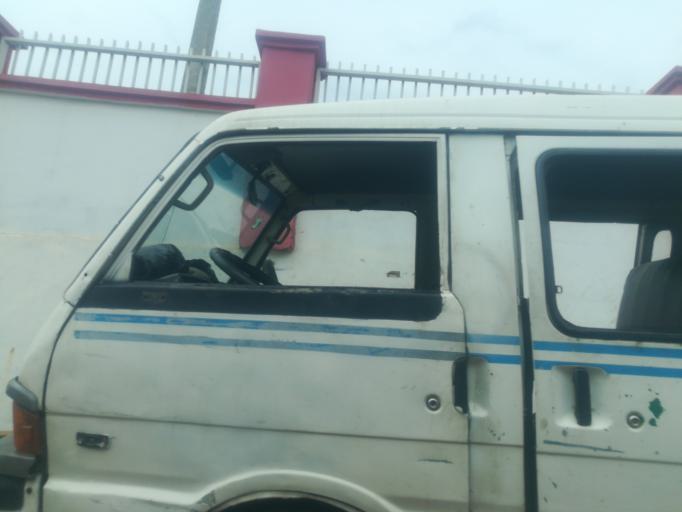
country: NG
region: Oyo
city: Ibadan
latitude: 7.4012
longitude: 3.9463
